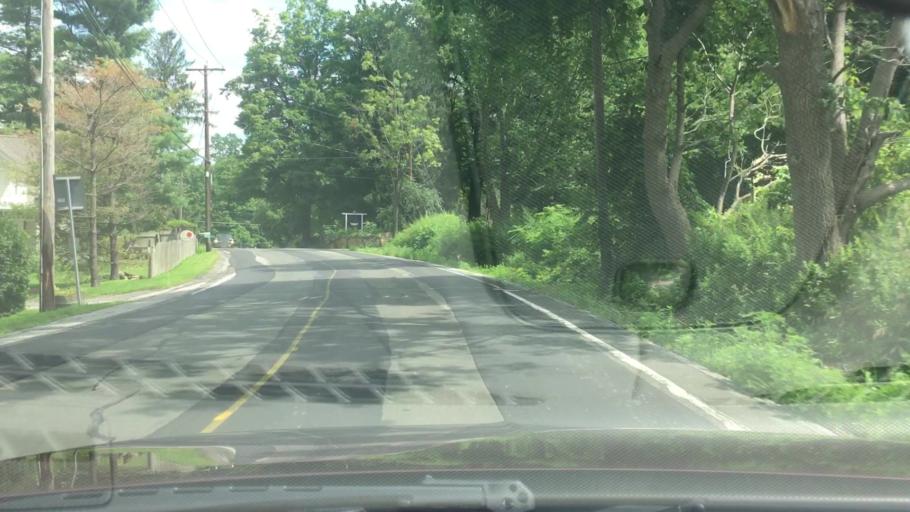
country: US
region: New York
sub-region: Dutchess County
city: Pawling
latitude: 41.6060
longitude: -73.6818
